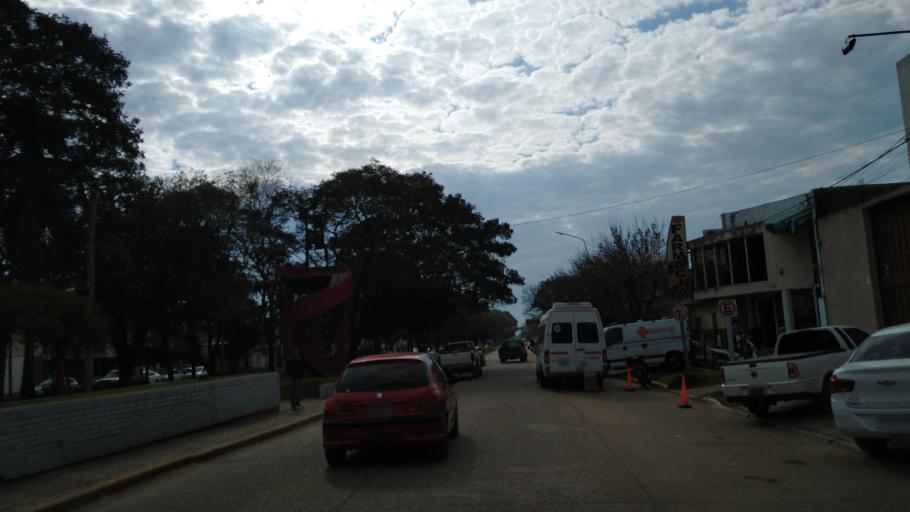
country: AR
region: Entre Rios
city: Chajari
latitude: -30.7590
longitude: -57.9889
